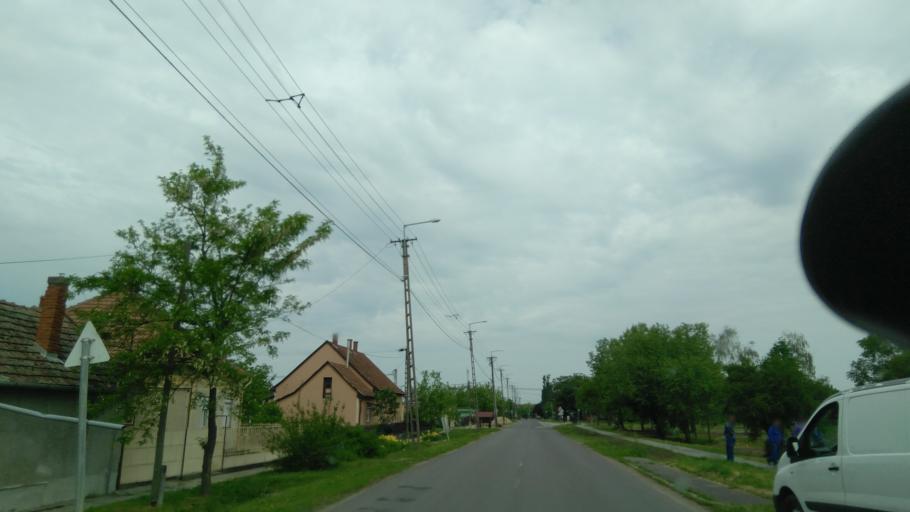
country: HU
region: Bekes
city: Szeghalom
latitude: 47.0338
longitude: 21.1635
